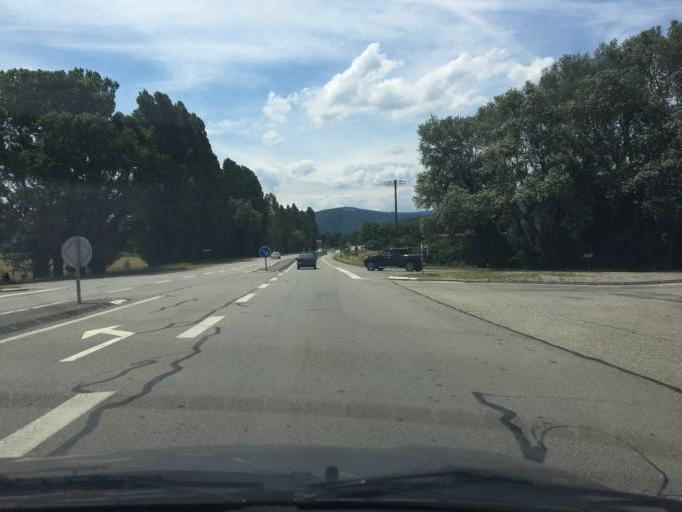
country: FR
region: Rhone-Alpes
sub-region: Departement de l'Ardeche
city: Charmes-sur-Rhone
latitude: 44.8449
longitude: 4.8614
